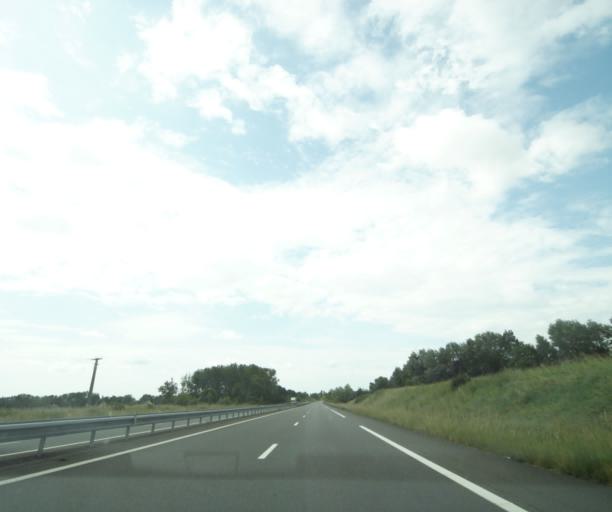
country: FR
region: Pays de la Loire
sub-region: Departement de Maine-et-Loire
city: Vivy
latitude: 47.3478
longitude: -0.0716
